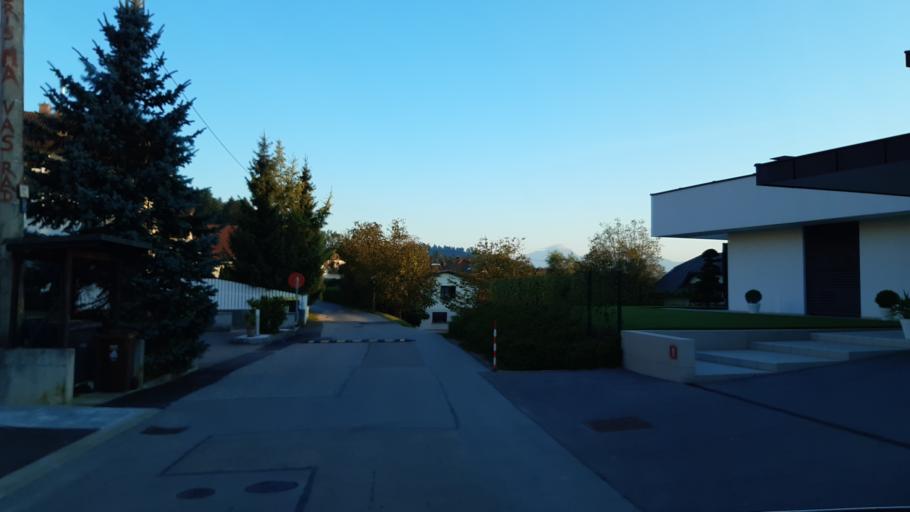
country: SI
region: Medvode
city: Zgornje Pirnice
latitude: 46.1092
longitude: 14.4363
